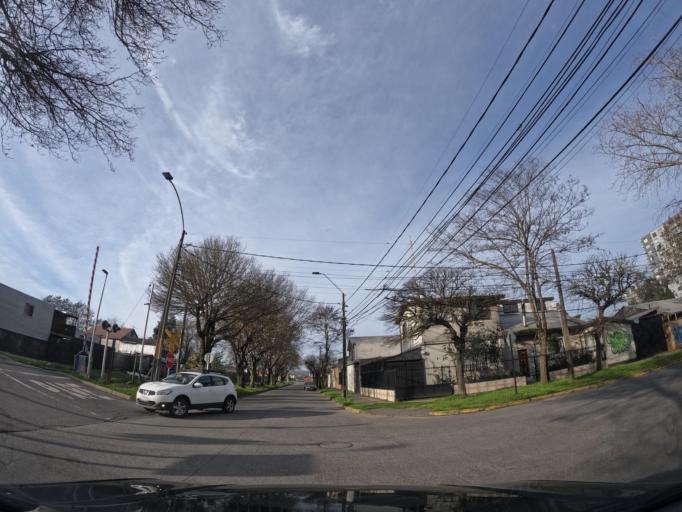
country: CL
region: Biobio
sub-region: Provincia de Concepcion
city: Concepcion
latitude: -36.8133
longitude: -73.0520
